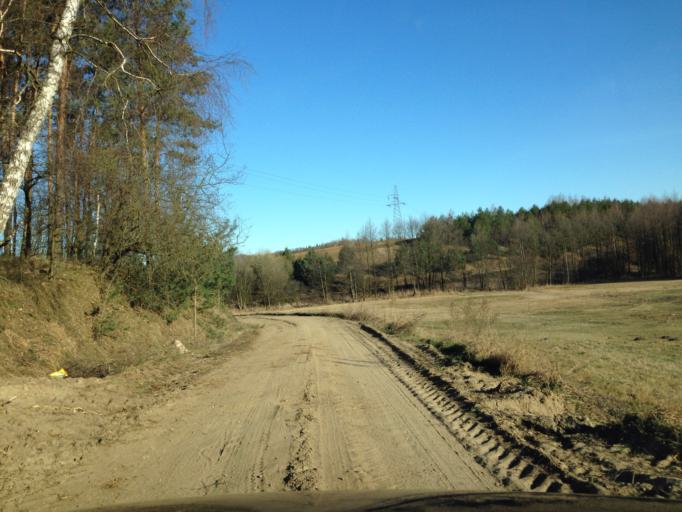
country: PL
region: Kujawsko-Pomorskie
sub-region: Powiat brodnicki
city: Brzozie
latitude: 53.3022
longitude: 19.6557
